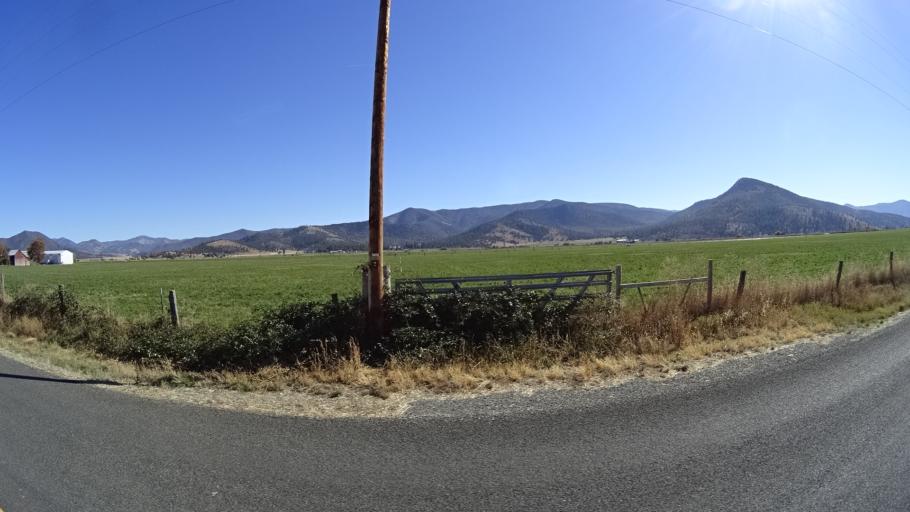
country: US
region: California
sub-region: Siskiyou County
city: Yreka
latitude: 41.5451
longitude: -122.8530
